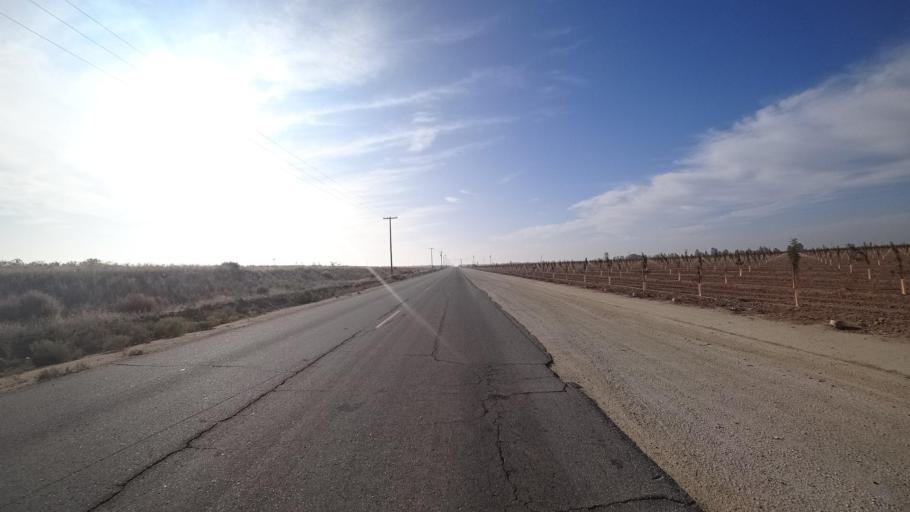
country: US
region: California
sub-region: Kern County
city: McFarland
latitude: 35.6490
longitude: -119.2046
